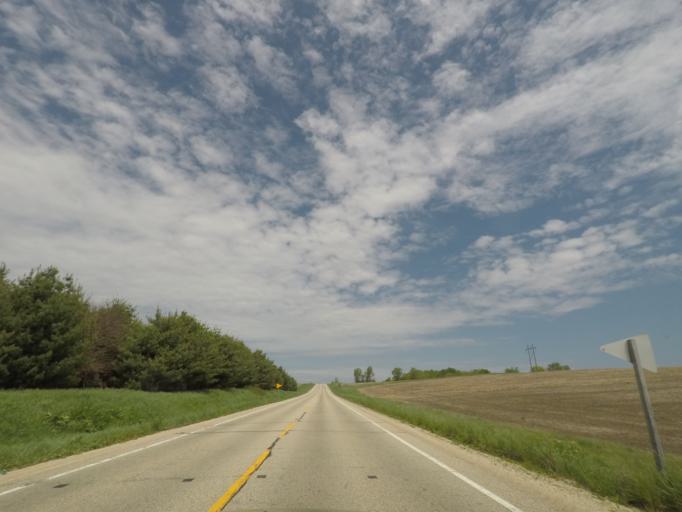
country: US
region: Wisconsin
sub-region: Rock County
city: Orfordville
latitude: 42.6640
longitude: -89.2883
